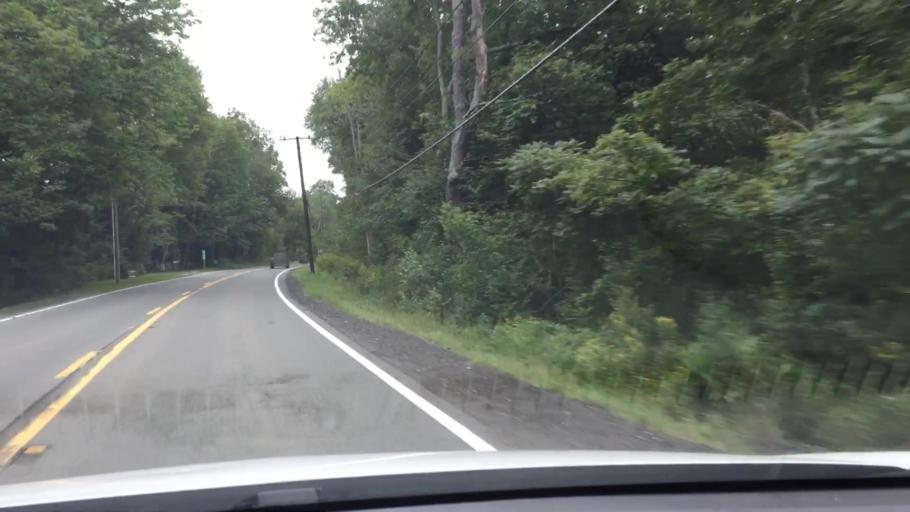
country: US
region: Massachusetts
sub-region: Berkshire County
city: Hinsdale
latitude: 42.3880
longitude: -73.1236
